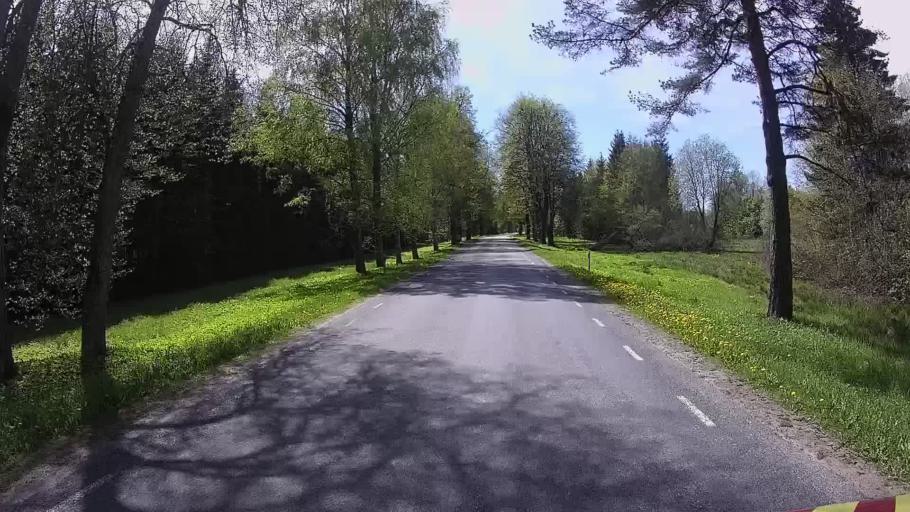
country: LV
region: Apes Novads
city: Ape
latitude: 57.6180
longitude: 26.5898
